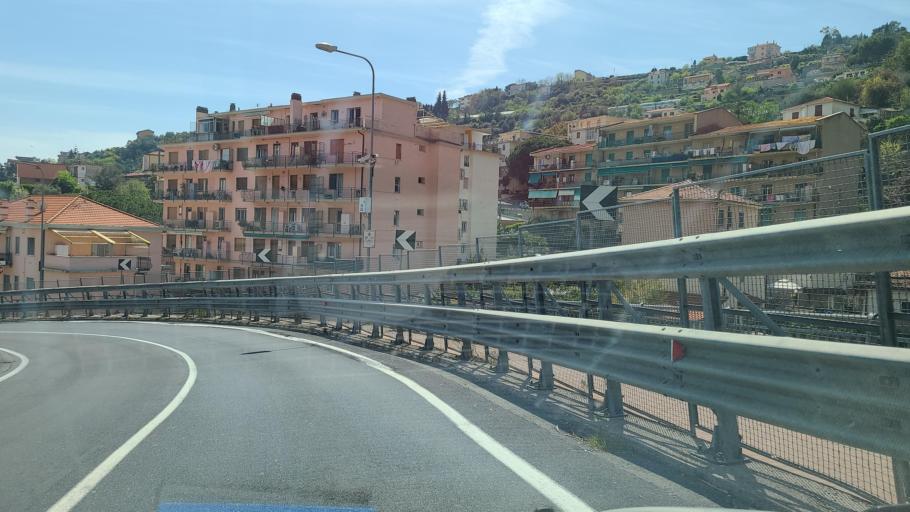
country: IT
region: Liguria
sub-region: Provincia di Imperia
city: San Remo
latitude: 43.8259
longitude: 7.7610
